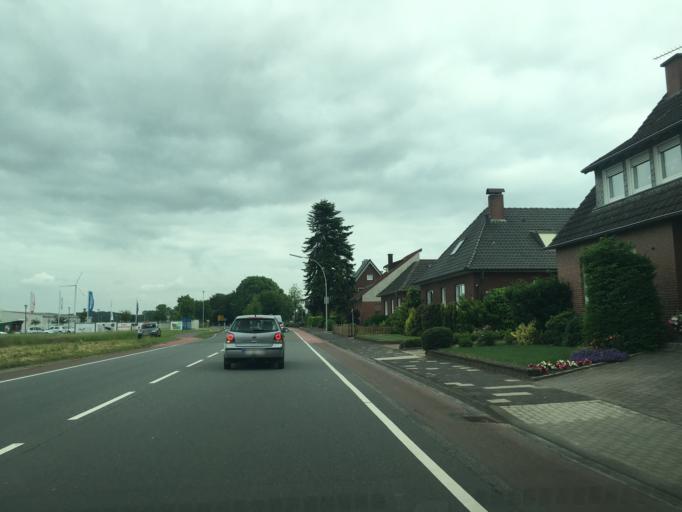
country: DE
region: North Rhine-Westphalia
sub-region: Regierungsbezirk Munster
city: Laer
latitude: 52.0560
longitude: 7.3660
